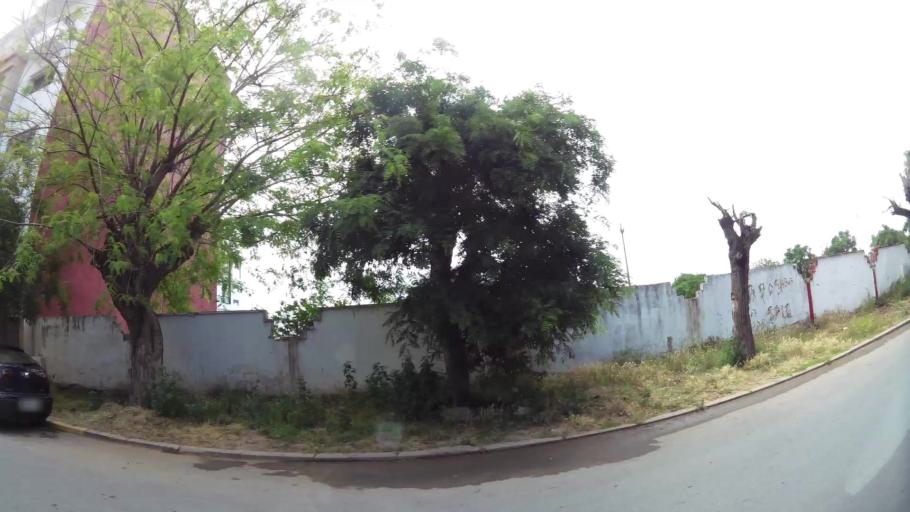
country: MA
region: Gharb-Chrarda-Beni Hssen
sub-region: Kenitra Province
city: Kenitra
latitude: 34.2543
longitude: -6.5887
